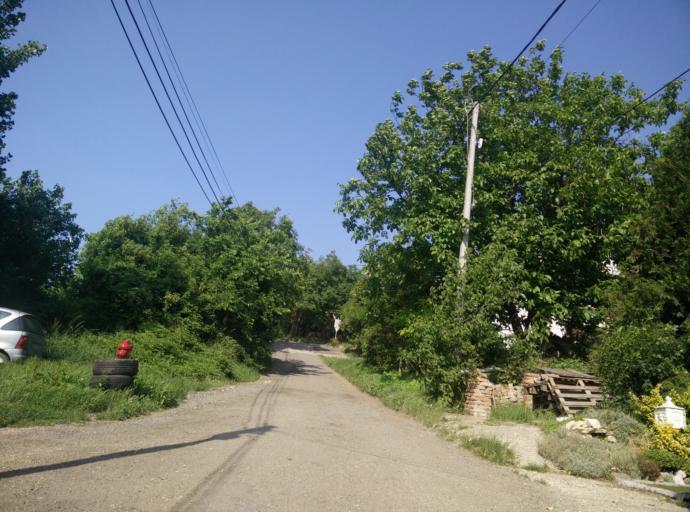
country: HU
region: Pest
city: Biatorbagy
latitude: 47.4751
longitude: 18.8147
